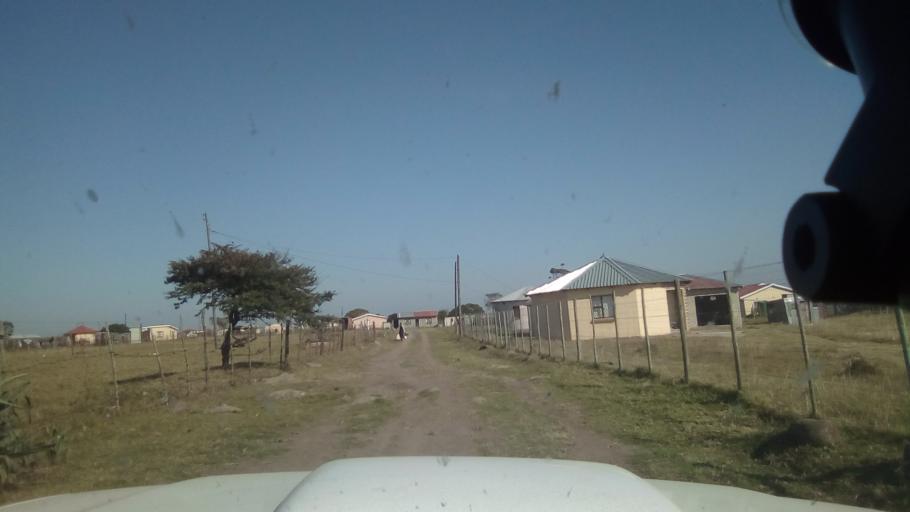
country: ZA
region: Eastern Cape
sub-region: Buffalo City Metropolitan Municipality
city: Bhisho
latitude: -32.9388
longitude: 27.3374
